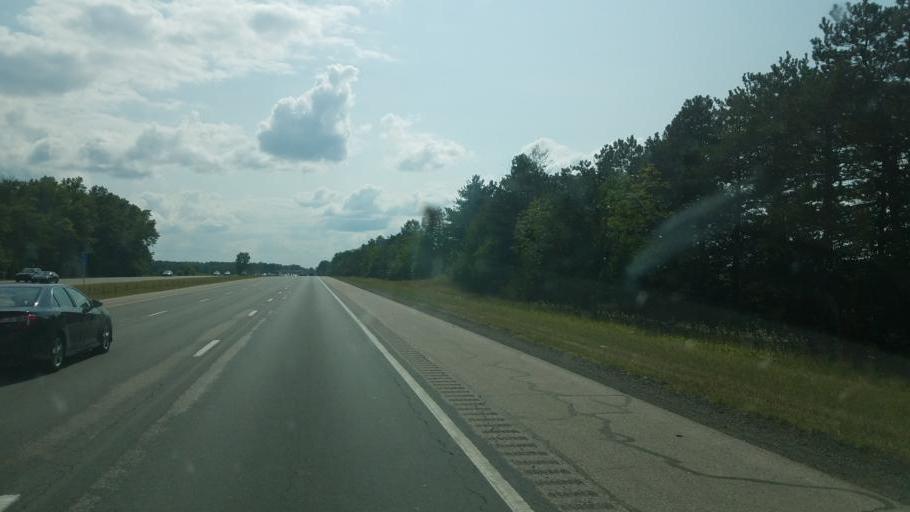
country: US
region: Ohio
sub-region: Wayne County
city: West Salem
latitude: 40.8921
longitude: -82.1844
